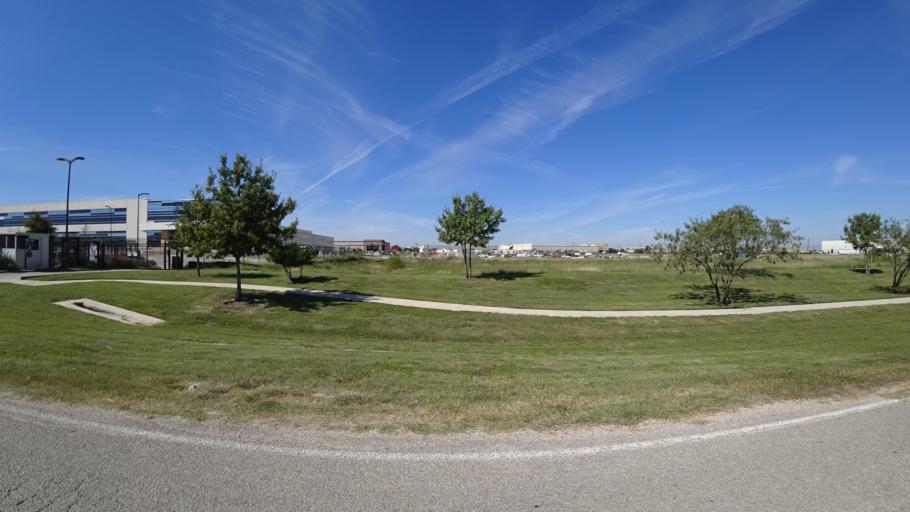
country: US
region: Texas
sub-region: Travis County
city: Austin
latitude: 30.1993
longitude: -97.7112
